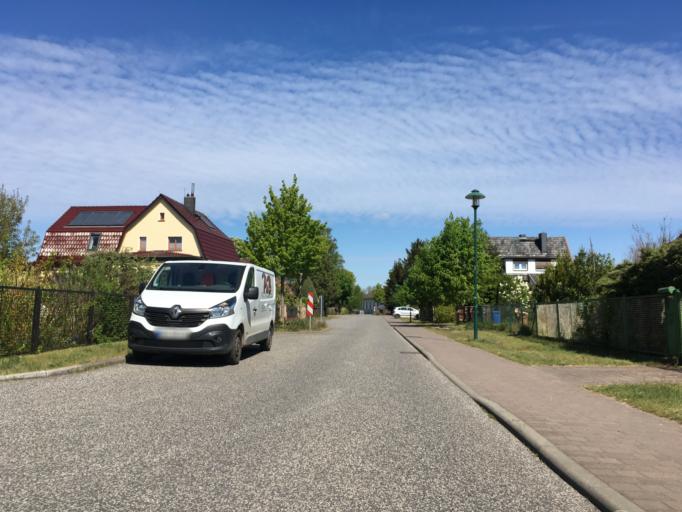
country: DE
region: Berlin
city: Buch
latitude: 52.6724
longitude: 13.5307
